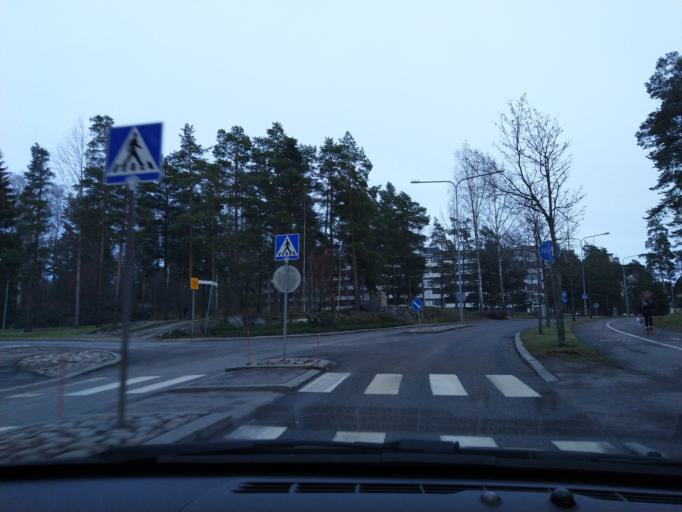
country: FI
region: Uusimaa
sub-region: Helsinki
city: Vantaa
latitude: 60.2405
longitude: 25.0704
